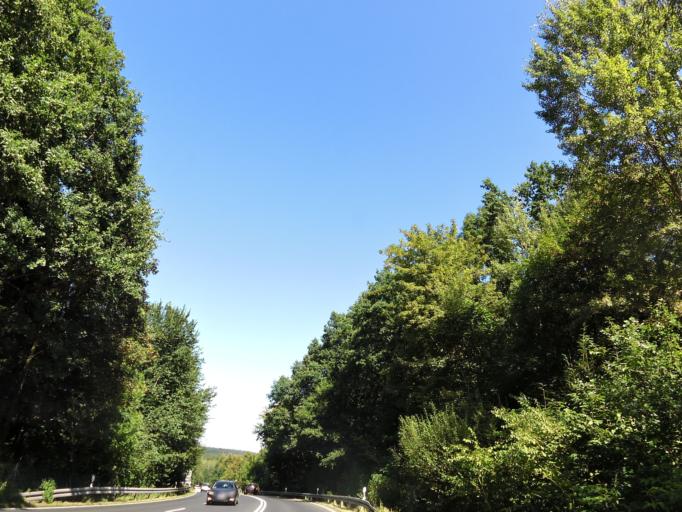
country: DE
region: Saxony
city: Konigstein
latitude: 50.9220
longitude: 14.0470
